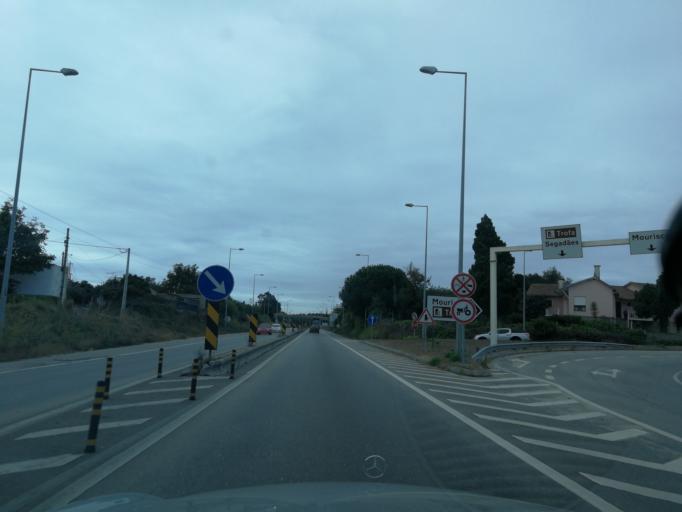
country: PT
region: Aveiro
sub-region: Agueda
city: Valongo
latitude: 40.6111
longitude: -8.4654
